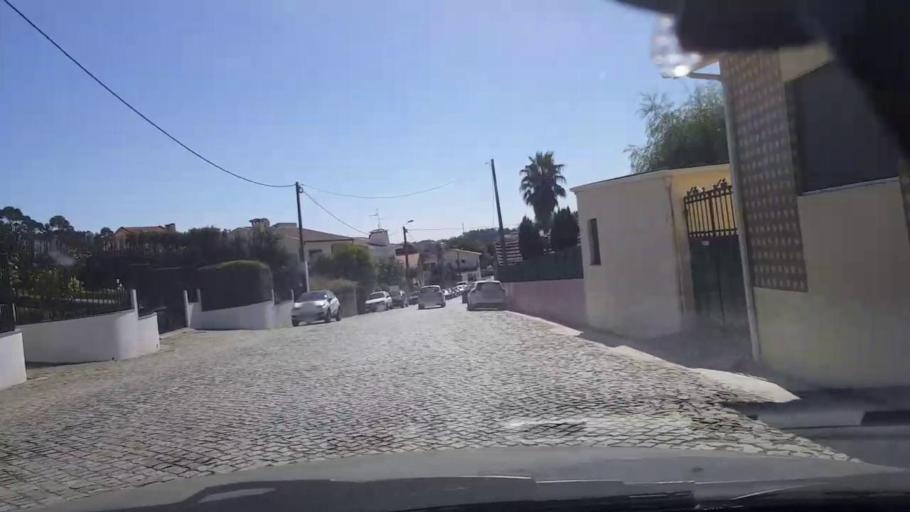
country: PT
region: Porto
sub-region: Vila do Conde
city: Arvore
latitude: 41.3205
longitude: -8.7237
